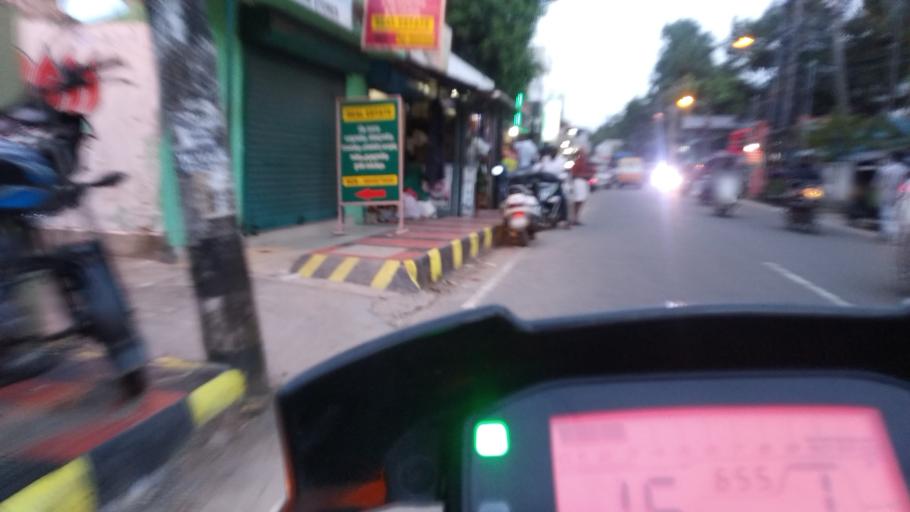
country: IN
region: Kerala
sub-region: Ernakulam
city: Elur
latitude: 10.0203
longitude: 76.2744
